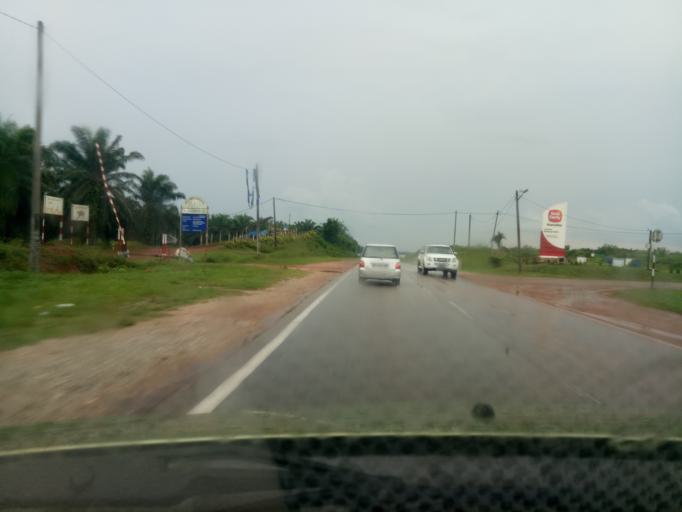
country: MY
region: Kedah
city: Sungai Petani
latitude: 5.5723
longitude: 100.5779
